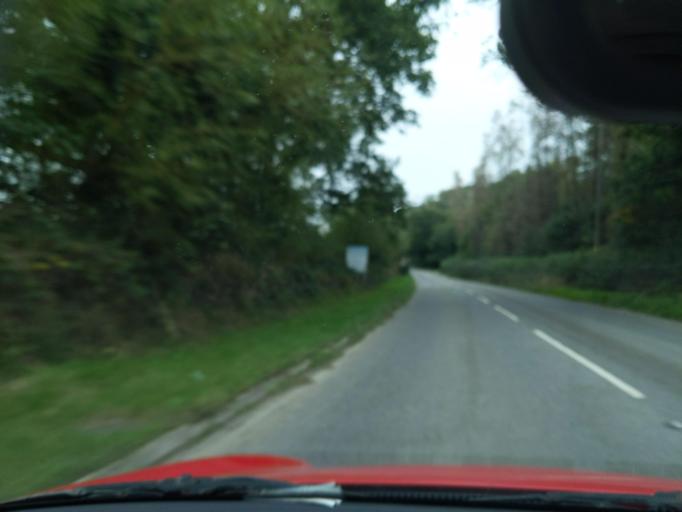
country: GB
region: England
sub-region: Devon
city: Okehampton
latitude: 50.8306
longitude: -4.0739
